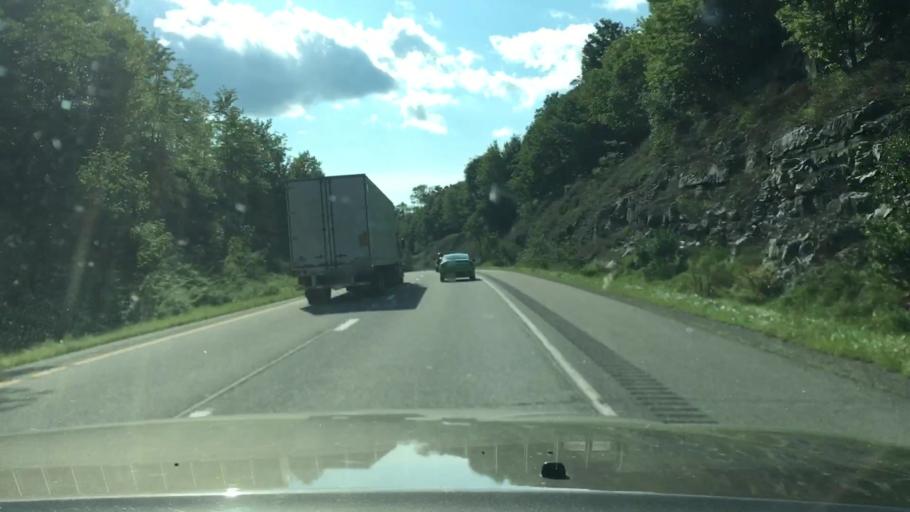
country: US
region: Pennsylvania
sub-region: Wayne County
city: Hawley
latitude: 41.3514
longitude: -75.2550
